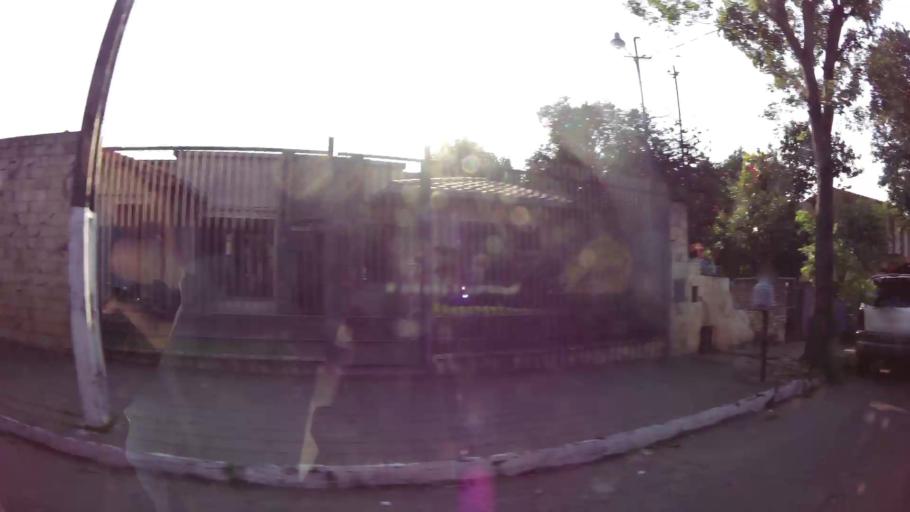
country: PY
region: Central
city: Lambare
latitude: -25.3421
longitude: -57.5995
